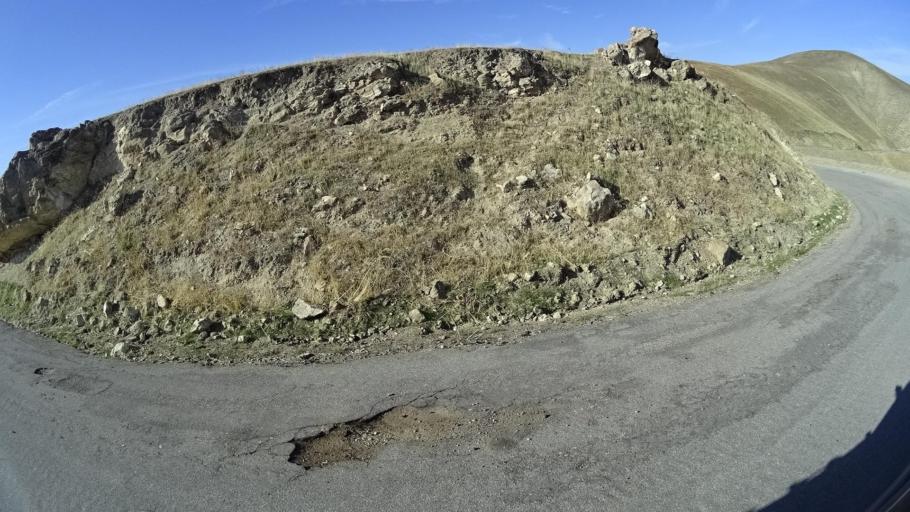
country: US
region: California
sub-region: Kern County
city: Arvin
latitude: 35.4026
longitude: -118.7712
